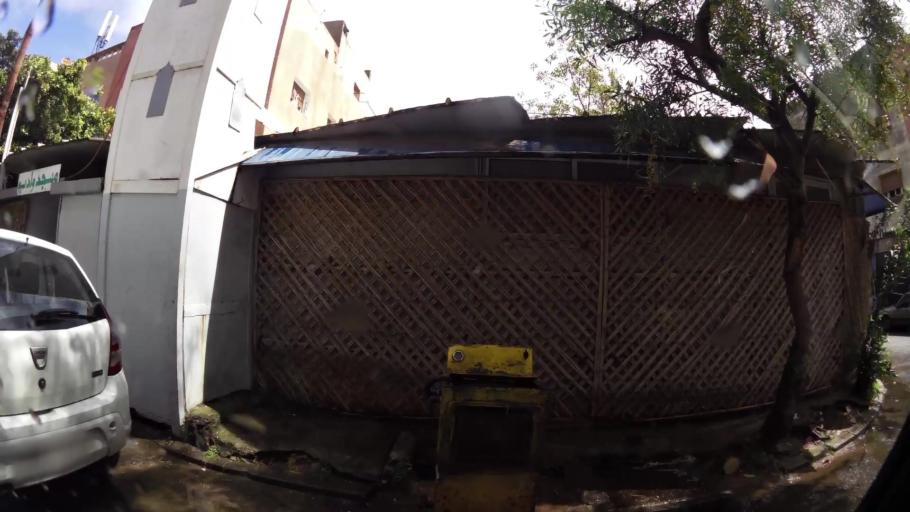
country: MA
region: Grand Casablanca
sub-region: Casablanca
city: Casablanca
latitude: 33.5521
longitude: -7.6779
